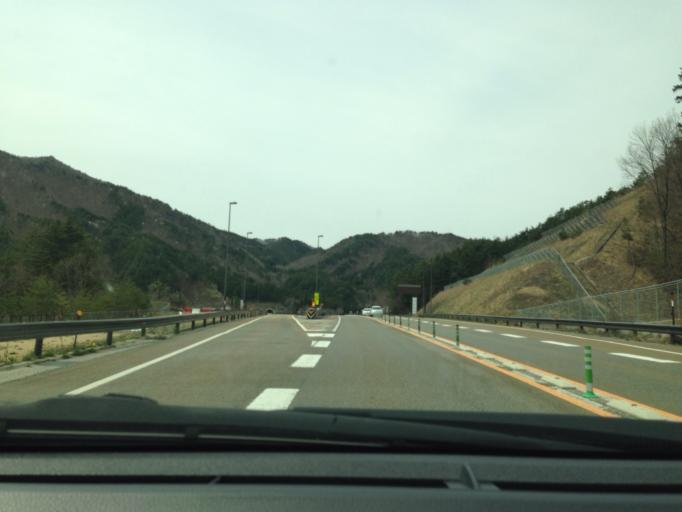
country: JP
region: Gifu
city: Takayama
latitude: 36.1405
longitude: 137.1479
